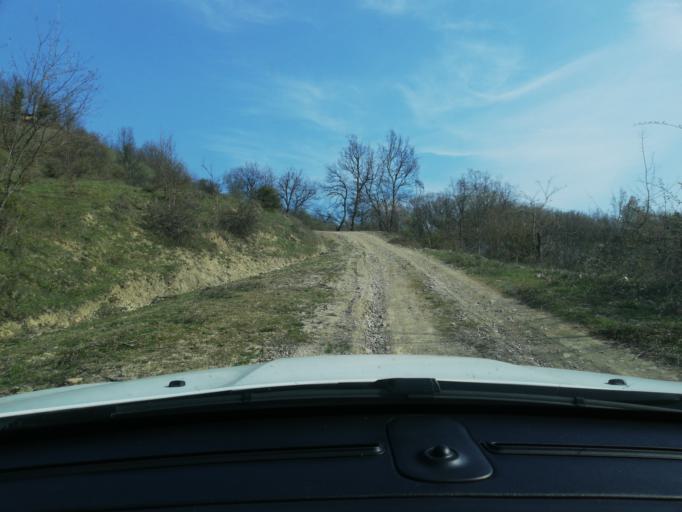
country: TR
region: Karabuk
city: Yenice
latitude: 41.2715
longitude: 32.3559
